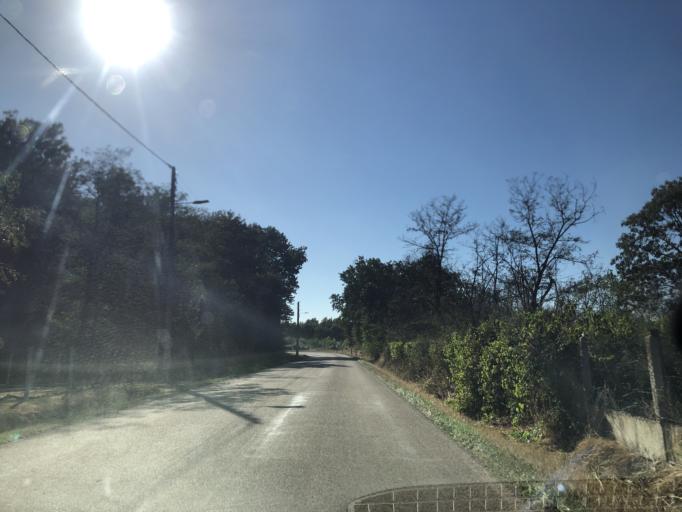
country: FR
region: Bourgogne
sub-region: Departement de l'Yonne
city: Cheny
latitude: 47.9276
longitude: 3.5446
